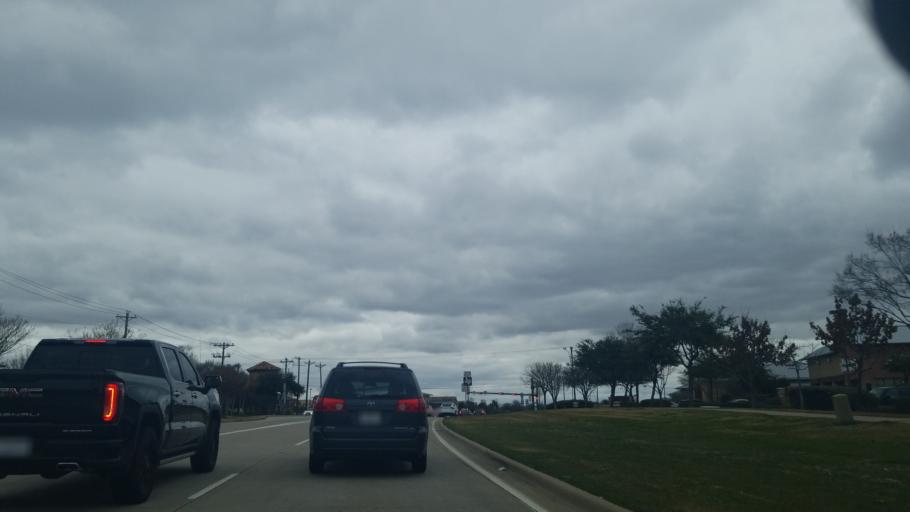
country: US
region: Texas
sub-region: Denton County
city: Double Oak
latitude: 33.0704
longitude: -97.0831
